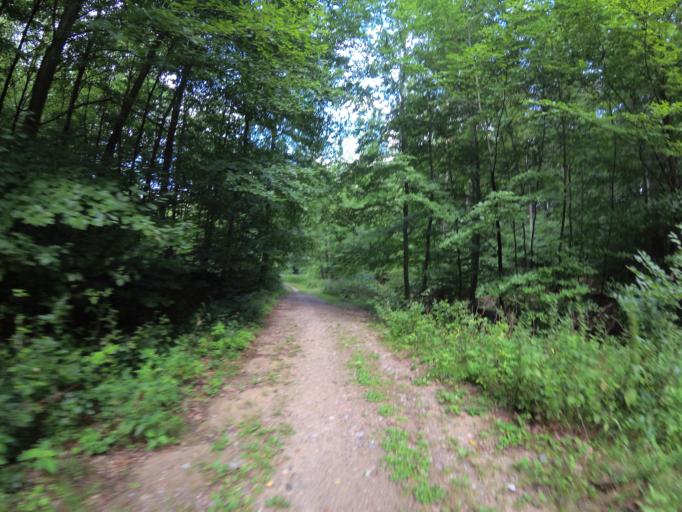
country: PL
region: Pomeranian Voivodeship
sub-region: Gdynia
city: Wielki Kack
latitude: 54.5099
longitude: 18.4464
